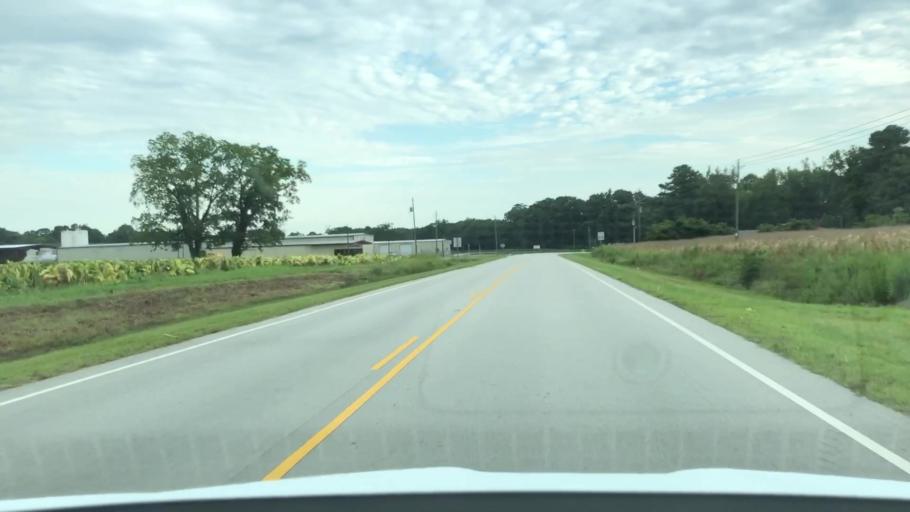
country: US
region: North Carolina
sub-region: Jones County
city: Trenton
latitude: 35.0542
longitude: -77.3564
